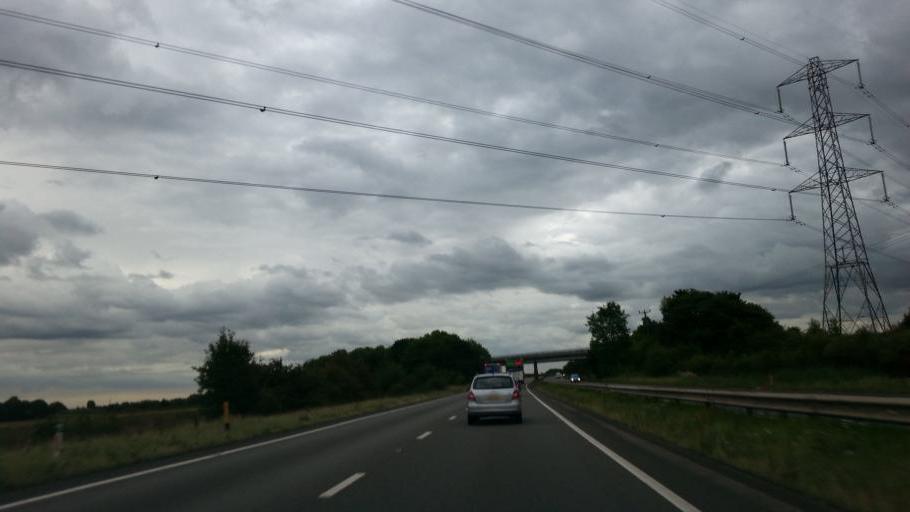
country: GB
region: England
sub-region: Nottinghamshire
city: South Collingham
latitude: 53.1857
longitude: -0.8267
